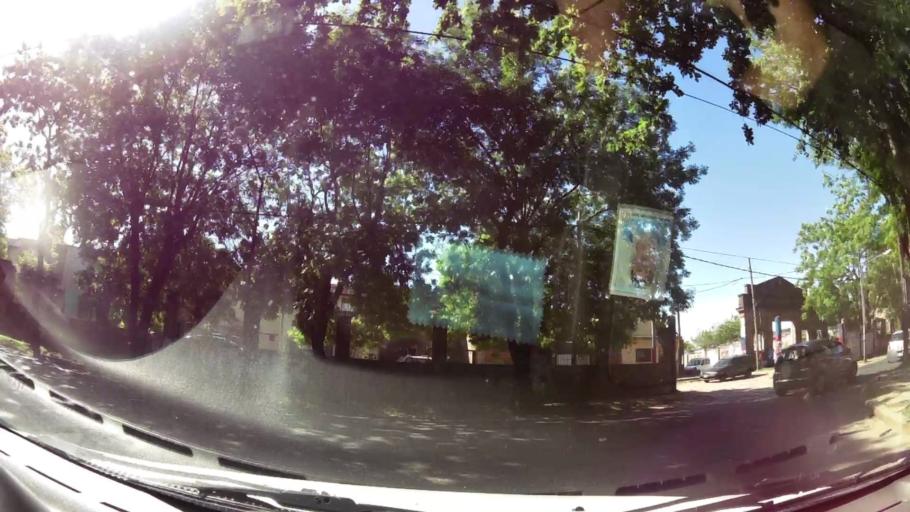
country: AR
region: Buenos Aires
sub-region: Partido de San Isidro
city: San Isidro
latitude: -34.4698
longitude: -58.5317
